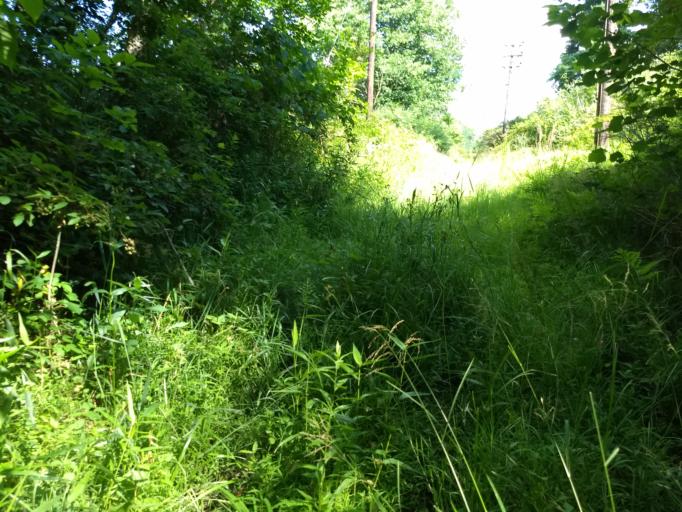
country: US
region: Pennsylvania
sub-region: Westmoreland County
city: Irwin
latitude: 40.3379
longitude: -79.7234
